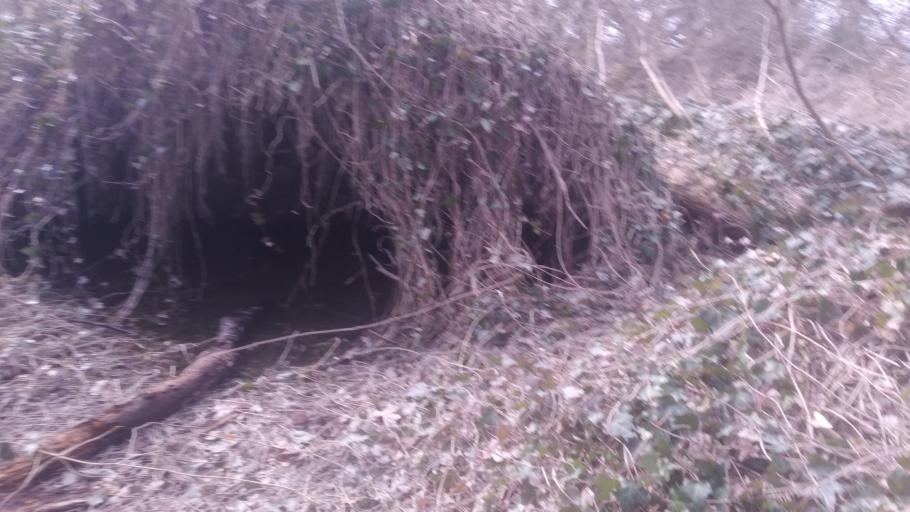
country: HU
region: Komarom-Esztergom
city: Tata
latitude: 47.6506
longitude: 18.3399
